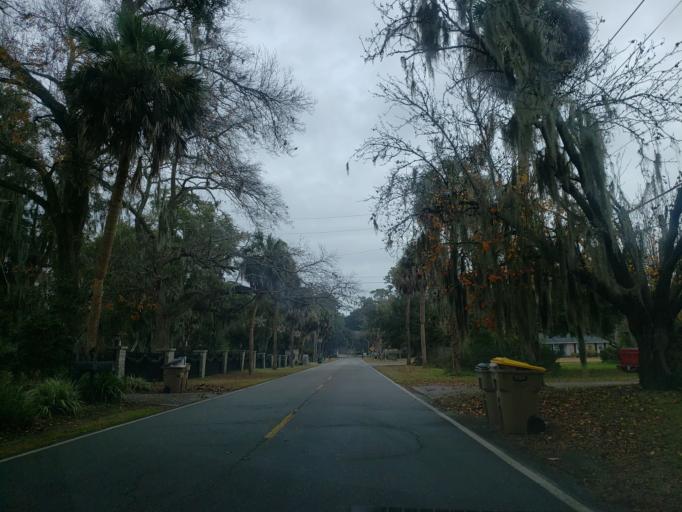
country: US
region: Georgia
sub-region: Chatham County
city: Wilmington Island
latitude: 31.9852
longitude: -80.9953
